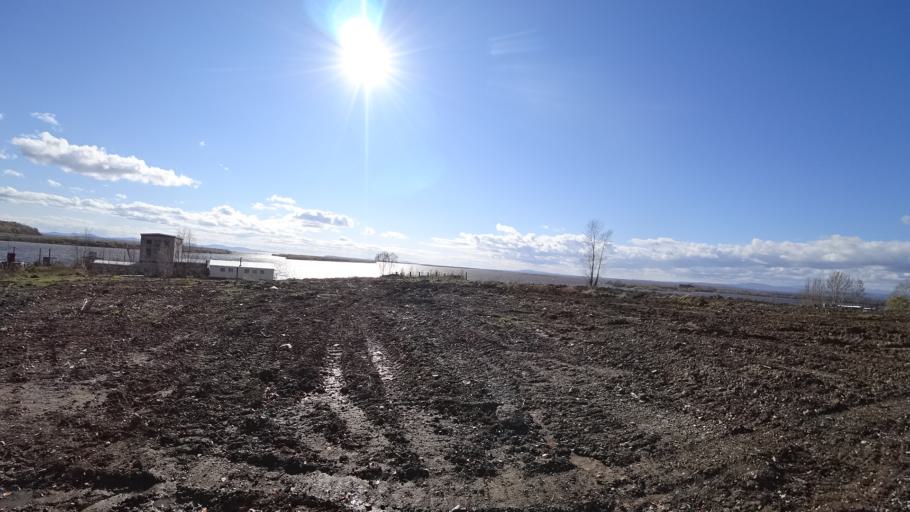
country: RU
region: Khabarovsk Krai
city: Amursk
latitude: 50.2147
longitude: 136.8894
